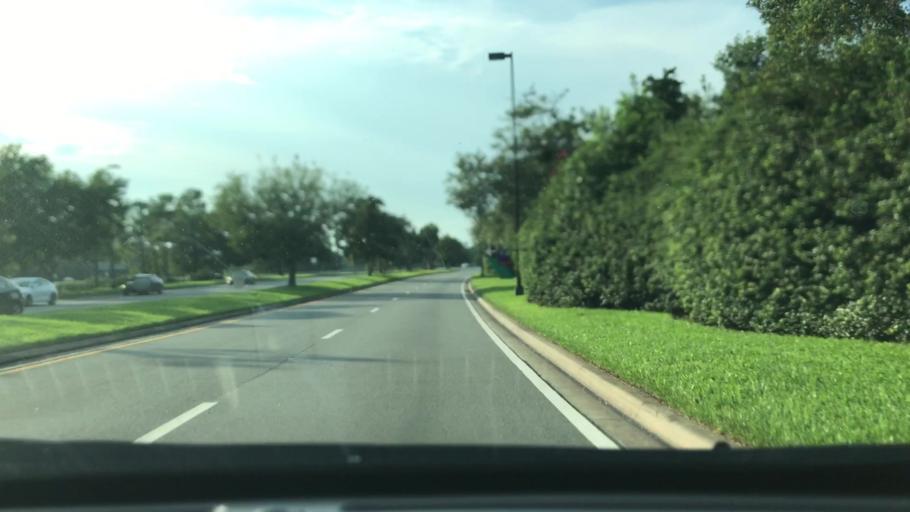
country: US
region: Florida
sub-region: Osceola County
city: Celebration
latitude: 28.3734
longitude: -81.5365
